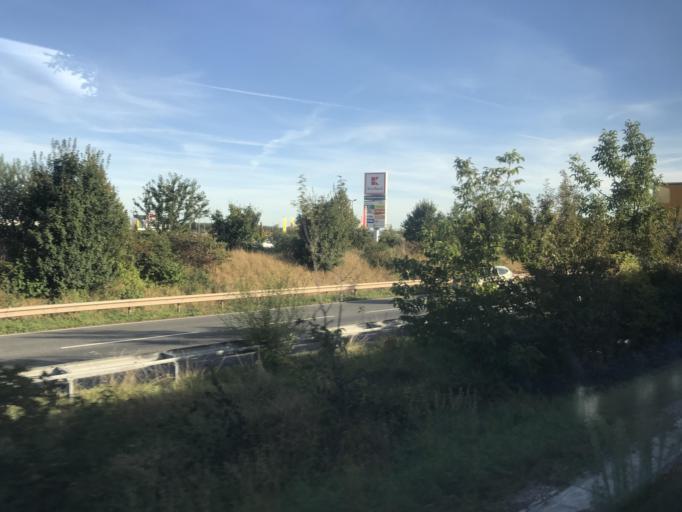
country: DE
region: Rheinland-Pfalz
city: Oppenheim
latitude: 49.8474
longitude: 8.3585
